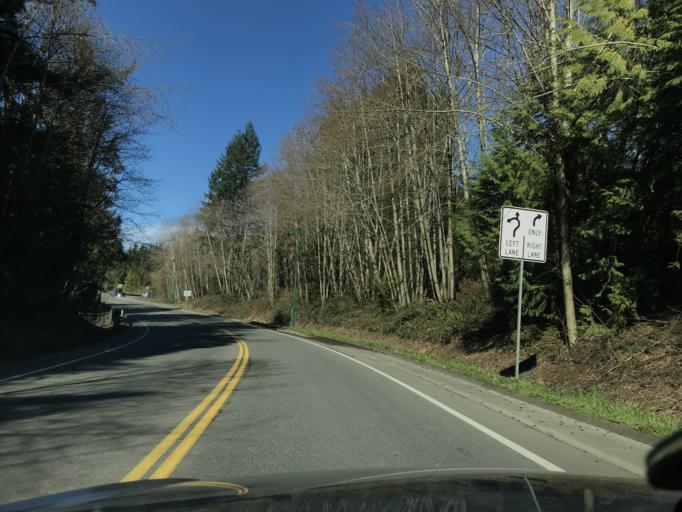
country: US
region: Washington
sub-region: Pierce County
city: Canterwood
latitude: 47.3567
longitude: -122.6118
